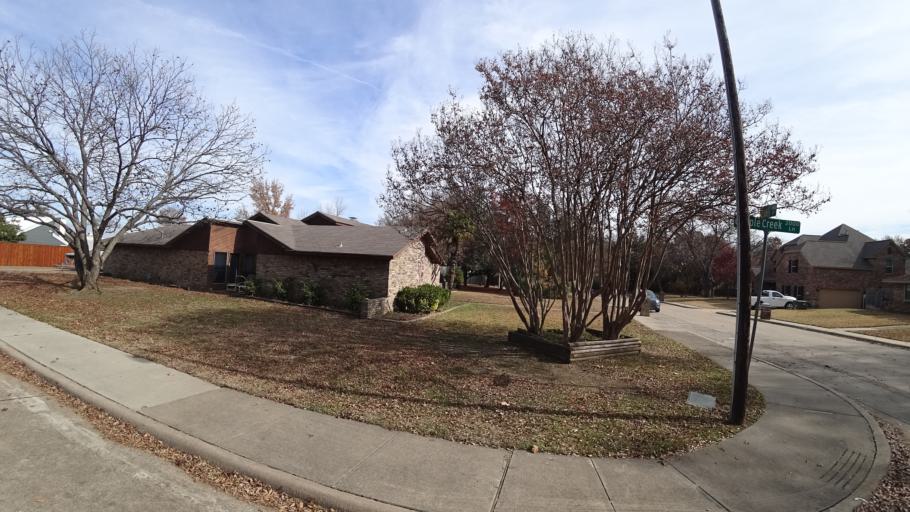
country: US
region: Texas
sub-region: Denton County
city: Highland Village
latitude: 33.0802
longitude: -97.0441
